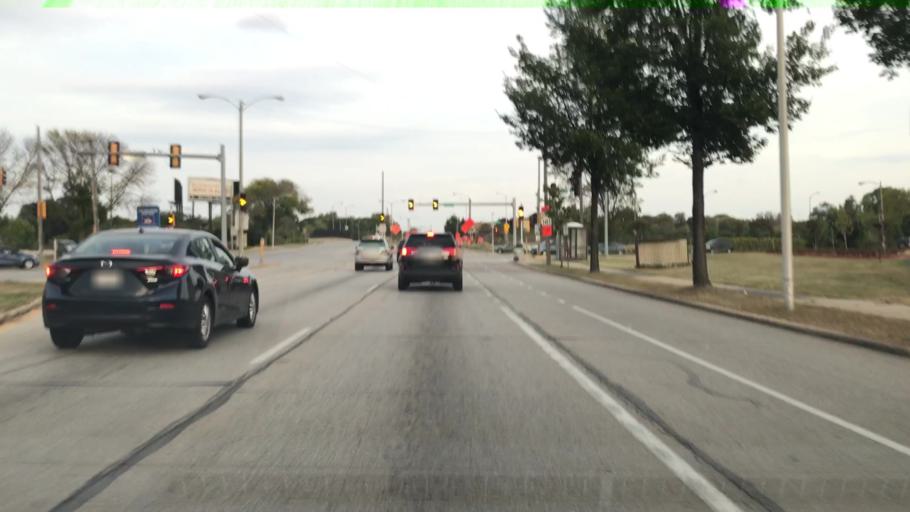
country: US
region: Wisconsin
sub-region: Waukesha County
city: Butler
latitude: 43.1195
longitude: -88.0149
